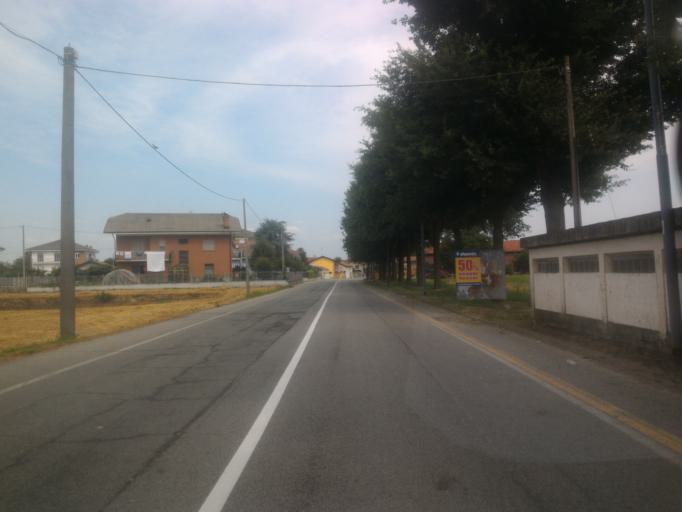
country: IT
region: Piedmont
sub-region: Provincia di Torino
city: Vigone
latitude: 44.8437
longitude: 7.4851
